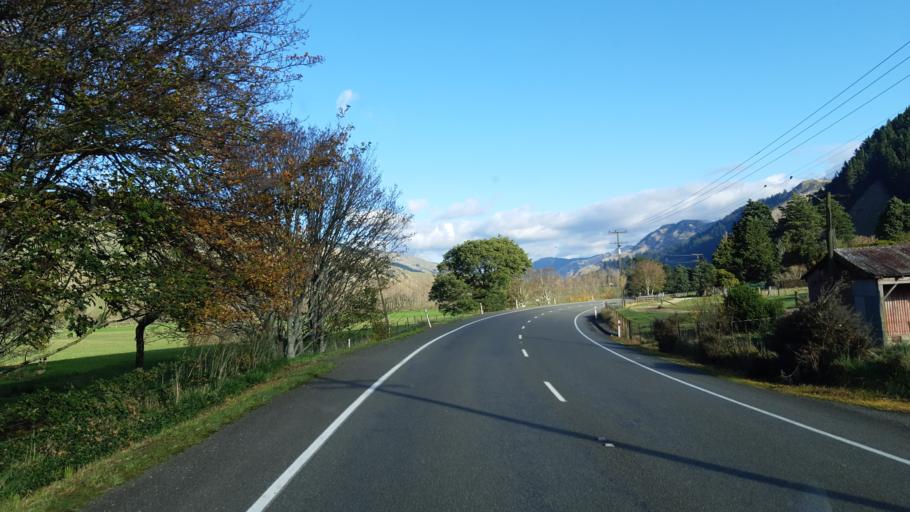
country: NZ
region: Marlborough
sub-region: Marlborough District
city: Picton
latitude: -41.3027
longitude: 173.7705
